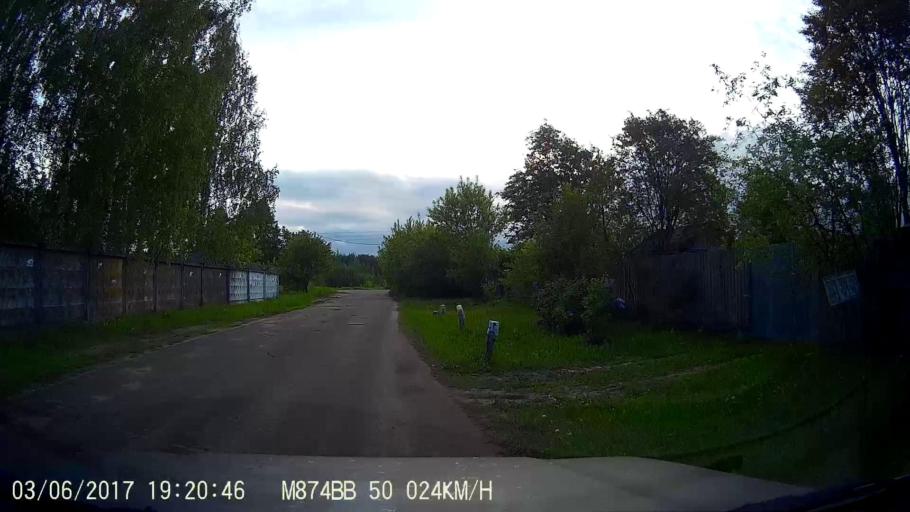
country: RU
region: Moskovskaya
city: Sychevo
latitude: 55.0672
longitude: 38.7245
